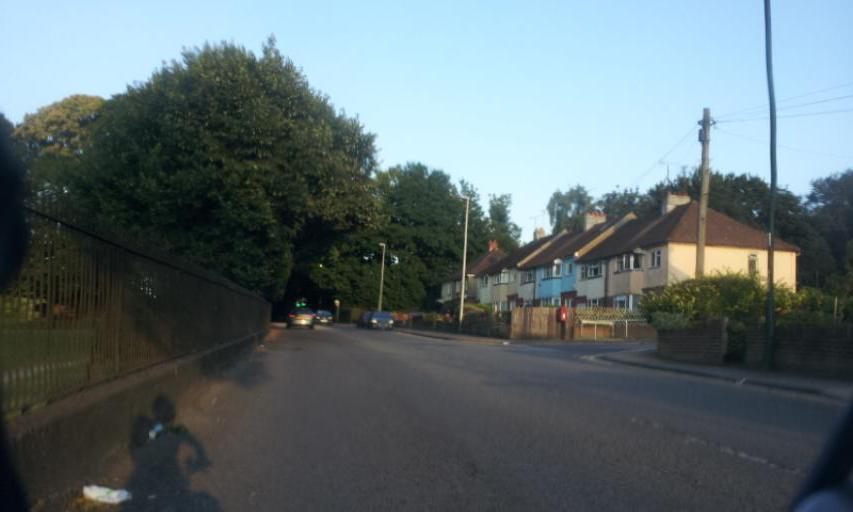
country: GB
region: England
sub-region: Kent
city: Gillingham
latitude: 51.3655
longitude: 0.5507
